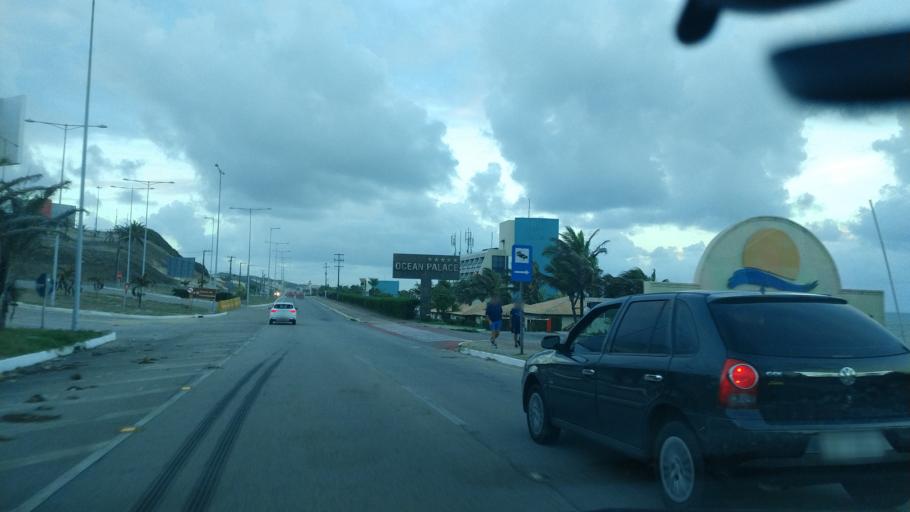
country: BR
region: Rio Grande do Norte
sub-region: Natal
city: Natal
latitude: -5.8642
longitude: -35.1808
